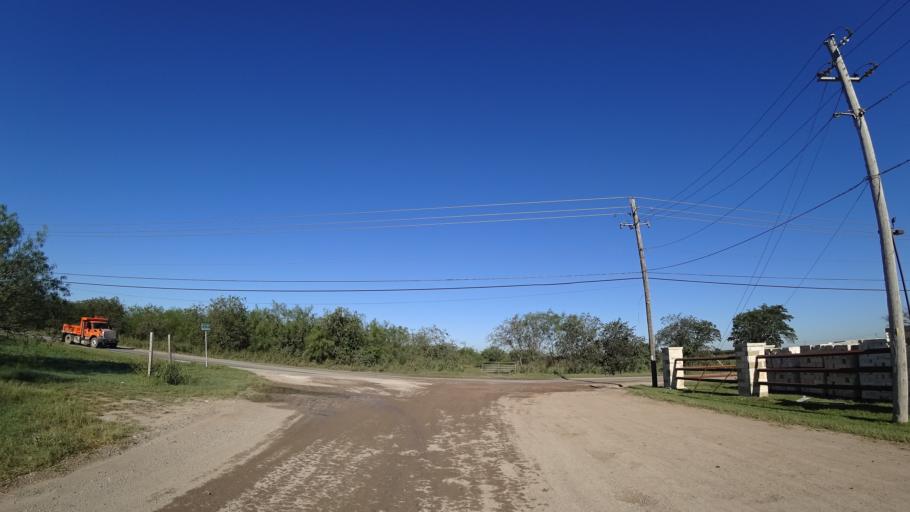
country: US
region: Texas
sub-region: Travis County
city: Hornsby Bend
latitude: 30.2354
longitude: -97.6644
